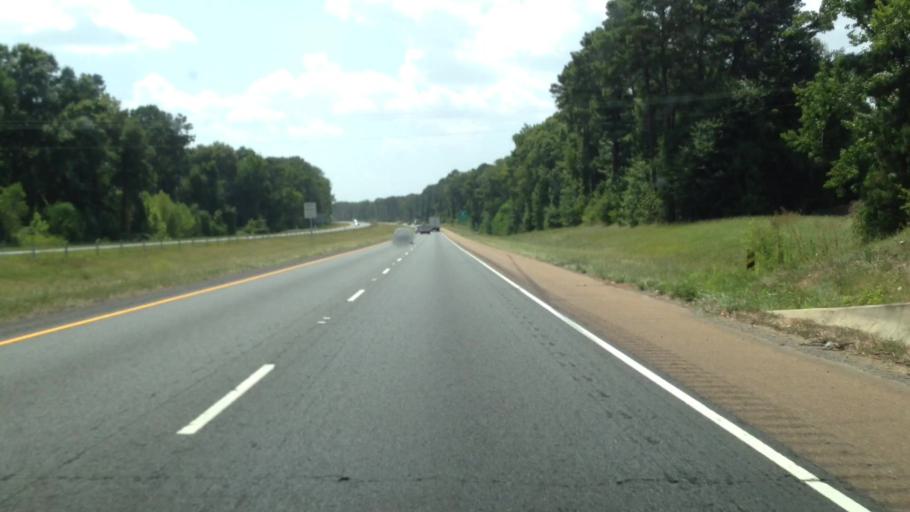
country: US
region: Louisiana
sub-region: Bienville Parish
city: Arcadia
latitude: 32.5659
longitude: -92.9209
